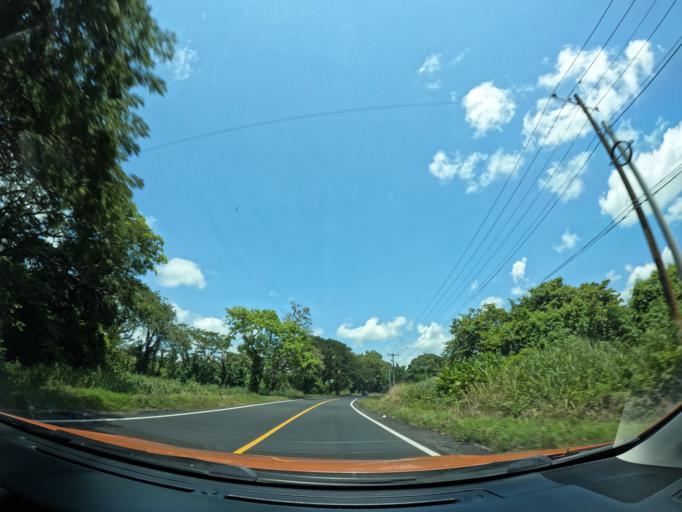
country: GT
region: Escuintla
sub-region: Municipio de Masagua
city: Masagua
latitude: 14.1810
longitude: -90.8660
